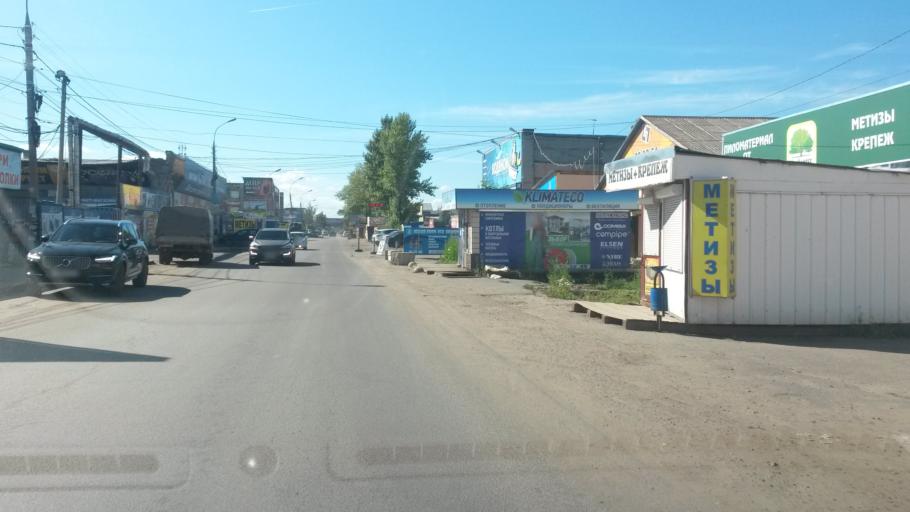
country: RU
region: Jaroslavl
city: Yaroslavl
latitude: 57.6180
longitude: 39.8440
